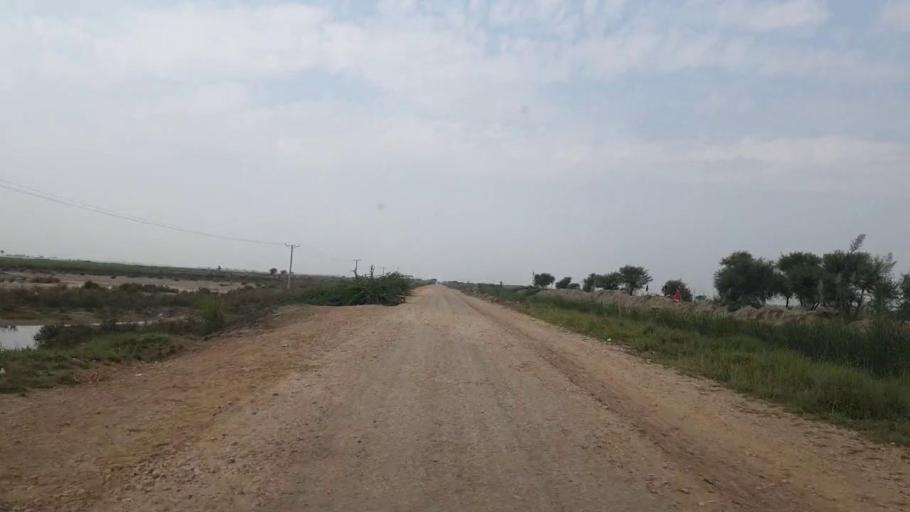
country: PK
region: Sindh
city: Kario
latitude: 24.6141
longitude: 68.5889
